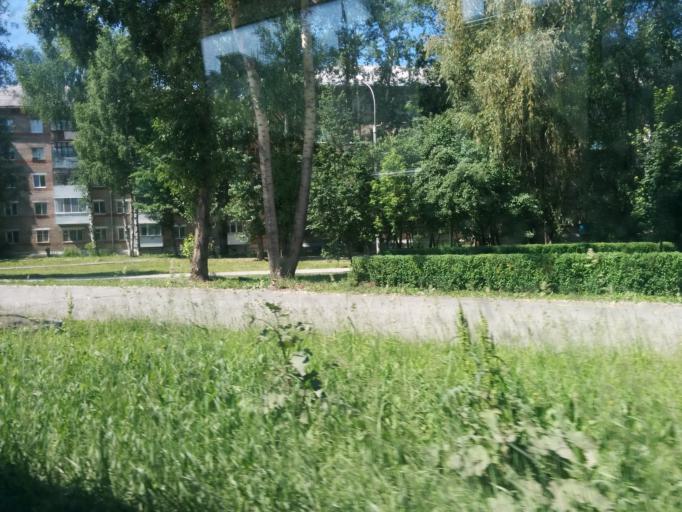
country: RU
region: Perm
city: Perm
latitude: 57.9995
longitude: 56.2958
